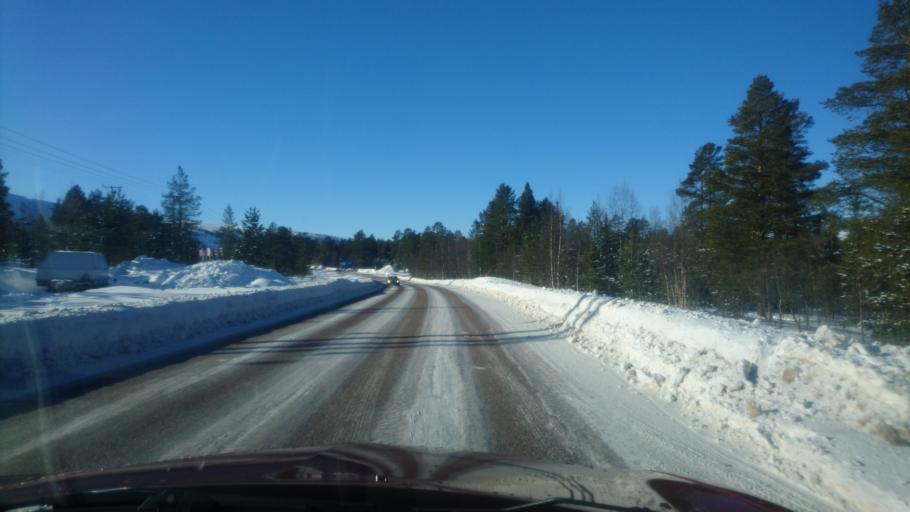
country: NO
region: Hedmark
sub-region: Trysil
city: Innbygda
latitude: 61.1813
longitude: 12.9978
